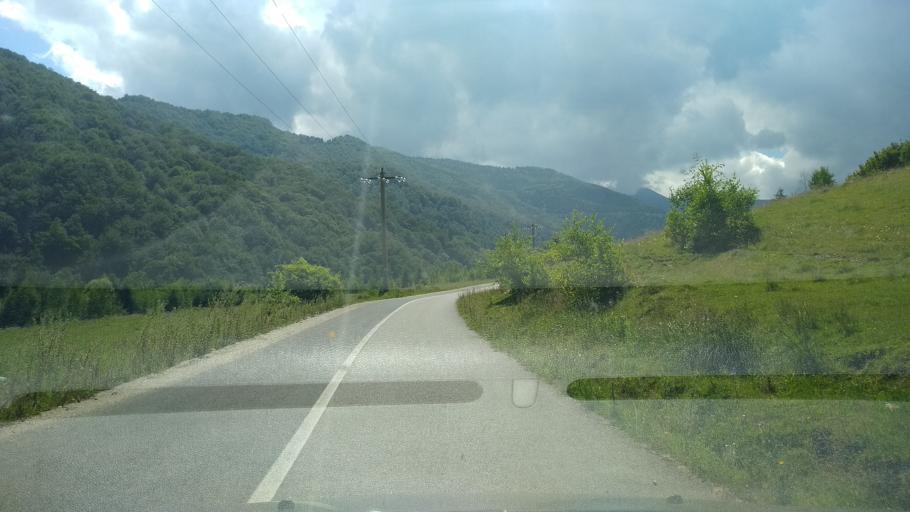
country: RO
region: Hunedoara
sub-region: Comuna Rau de Mori
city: Rau de Mori
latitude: 45.4620
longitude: 22.8977
